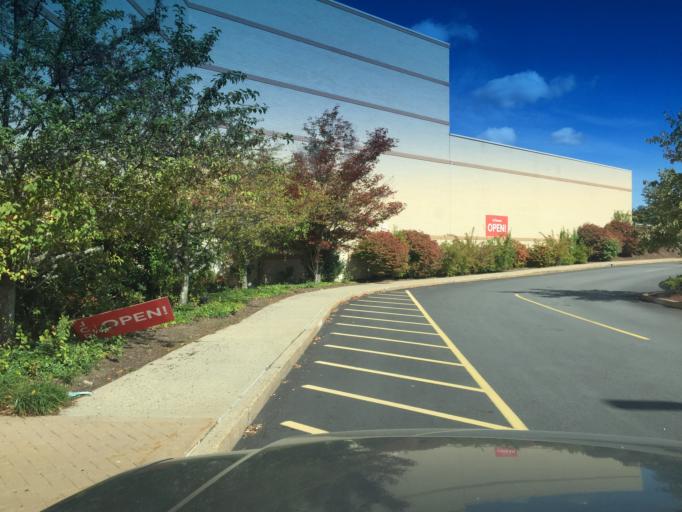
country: US
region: Massachusetts
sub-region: Worcester County
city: Berlin
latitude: 42.3562
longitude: -71.6113
